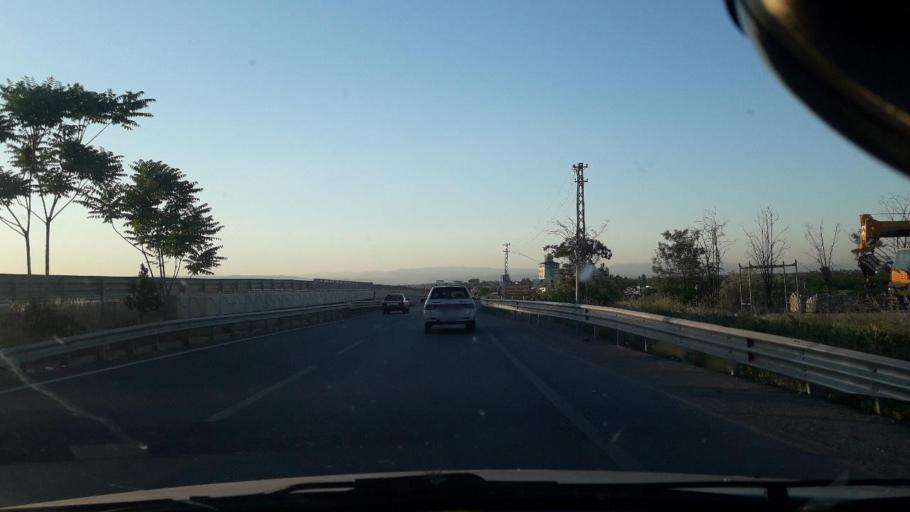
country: TR
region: Malatya
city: Yesilyurt
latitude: 38.3402
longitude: 38.2345
